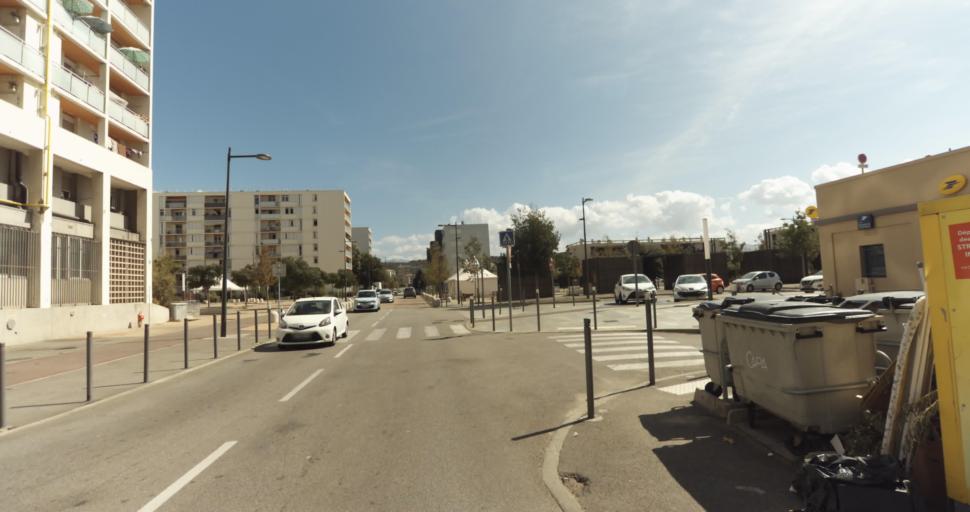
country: FR
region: Corsica
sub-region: Departement de la Corse-du-Sud
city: Ajaccio
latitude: 41.9352
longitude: 8.7472
